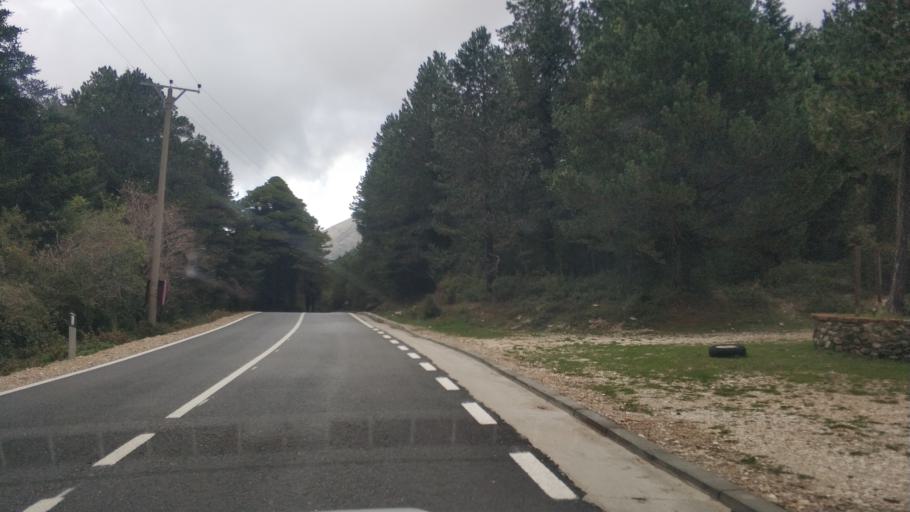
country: AL
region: Vlore
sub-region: Rrethi i Vlores
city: Brataj
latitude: 40.2113
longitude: 19.5791
